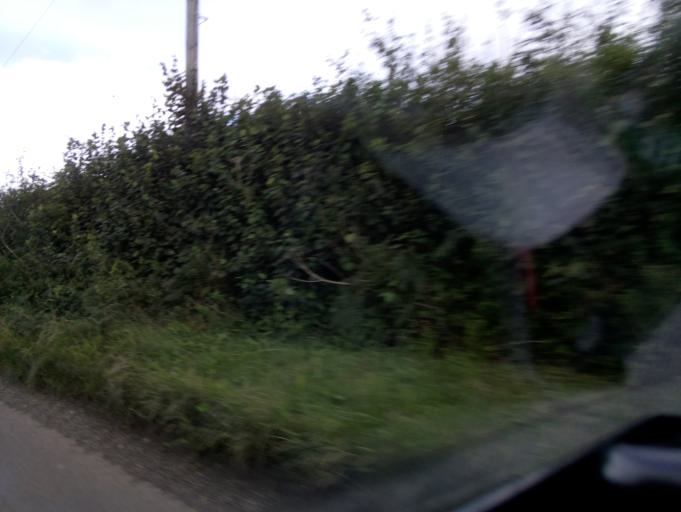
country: GB
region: England
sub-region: Devon
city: Kingsbridge
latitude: 50.2995
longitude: -3.7916
